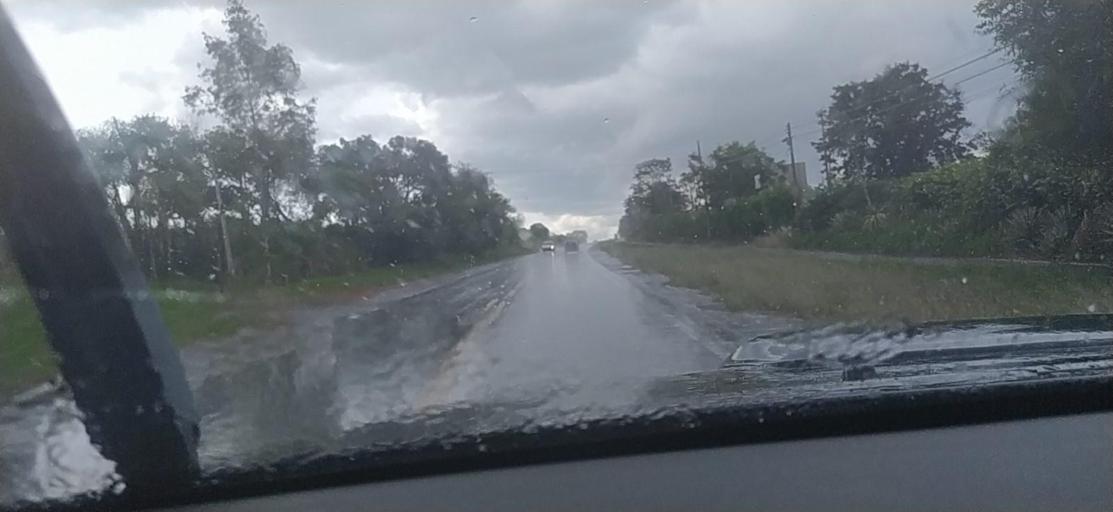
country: BR
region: Sao Paulo
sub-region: Catanduva
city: Catanduva
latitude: -21.1582
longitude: -48.9497
